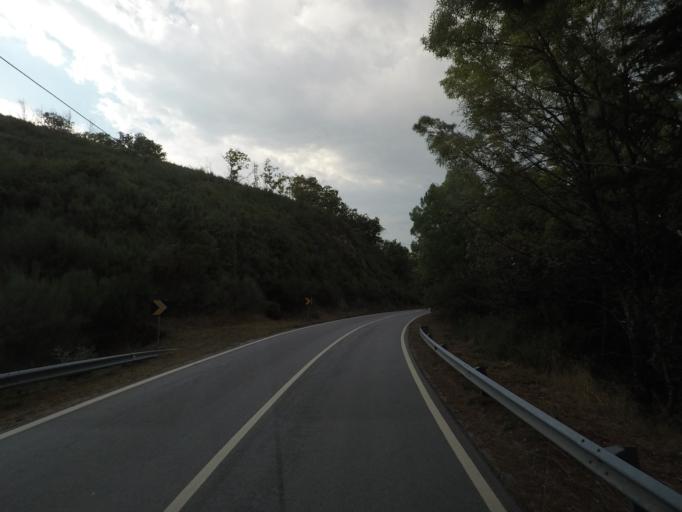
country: PT
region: Porto
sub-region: Baiao
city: Valadares
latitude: 41.2060
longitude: -7.9729
